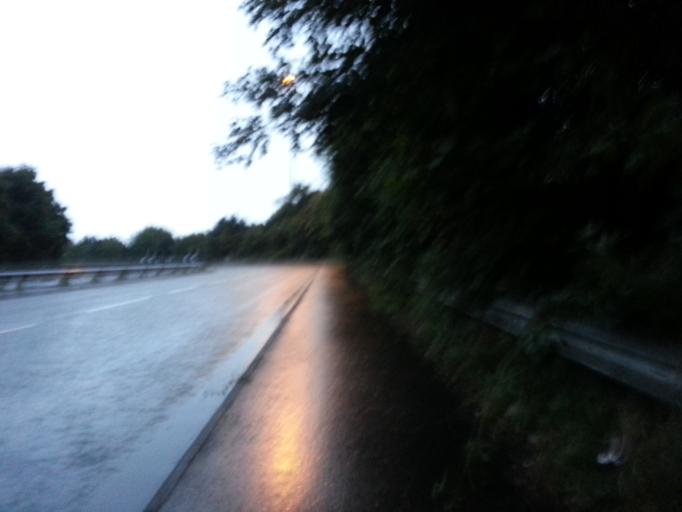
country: GB
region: Northern Ireland
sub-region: Newtownabbey District
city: Newtownabbey
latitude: 54.6308
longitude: -5.9218
